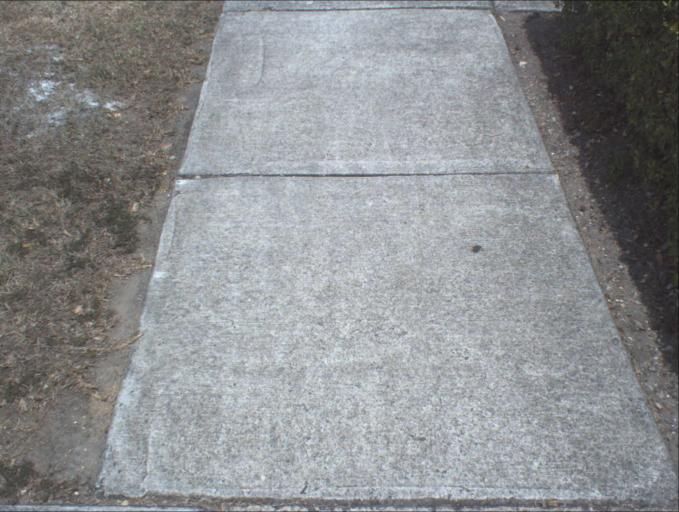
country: AU
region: Queensland
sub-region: Logan
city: Slacks Creek
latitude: -27.6657
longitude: 153.1859
